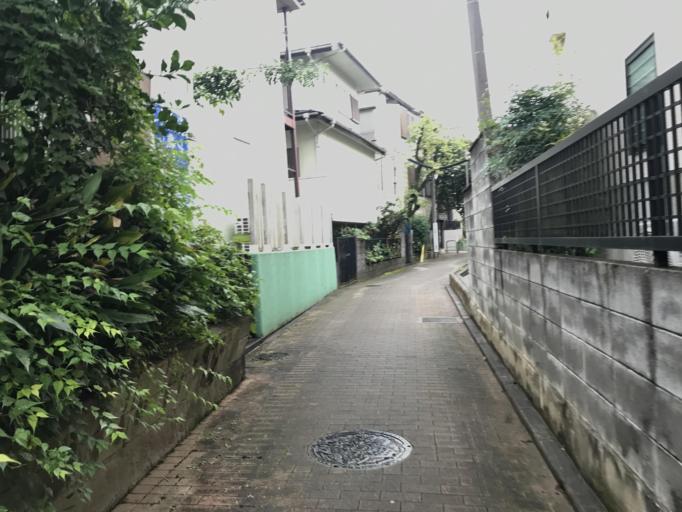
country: JP
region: Saitama
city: Wako
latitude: 35.7417
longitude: 139.6405
